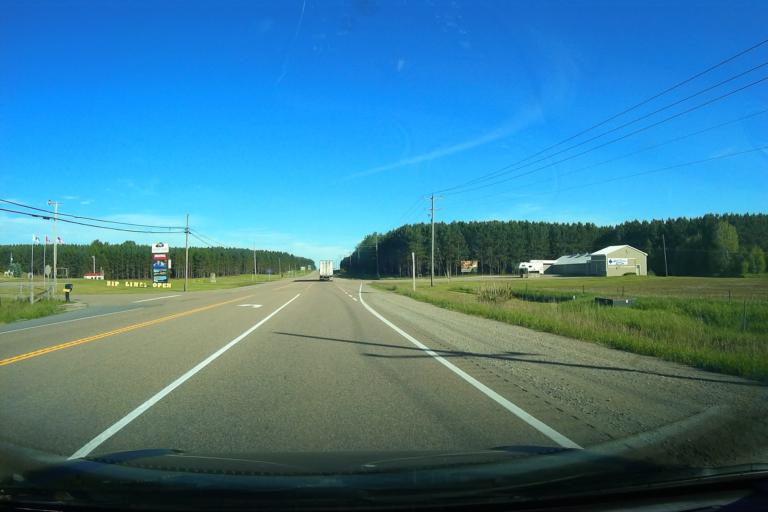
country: CA
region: Ontario
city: Renfrew
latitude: 45.5993
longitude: -76.8455
